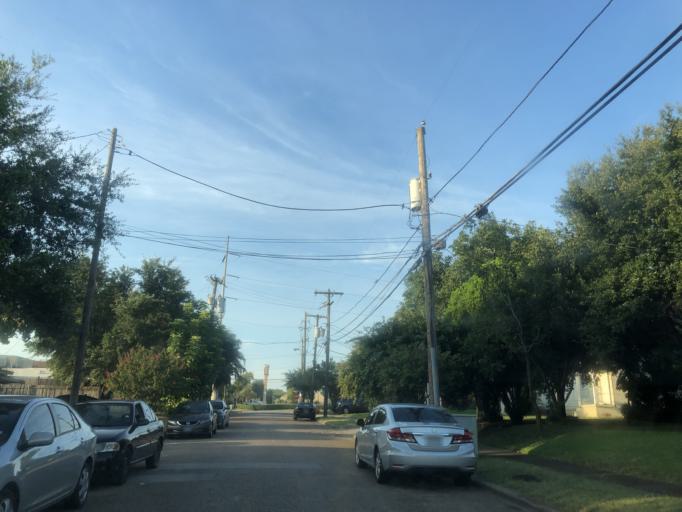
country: US
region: Texas
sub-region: Dallas County
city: Cockrell Hill
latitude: 32.7506
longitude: -96.8581
